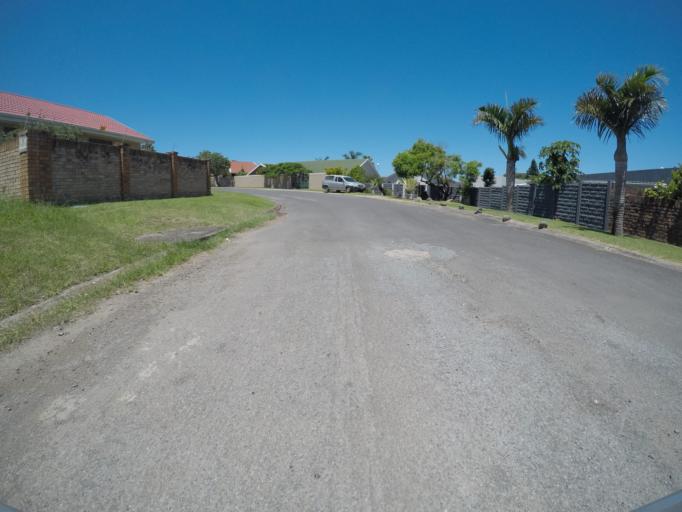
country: ZA
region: Eastern Cape
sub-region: Buffalo City Metropolitan Municipality
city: East London
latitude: -32.9585
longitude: 27.9360
